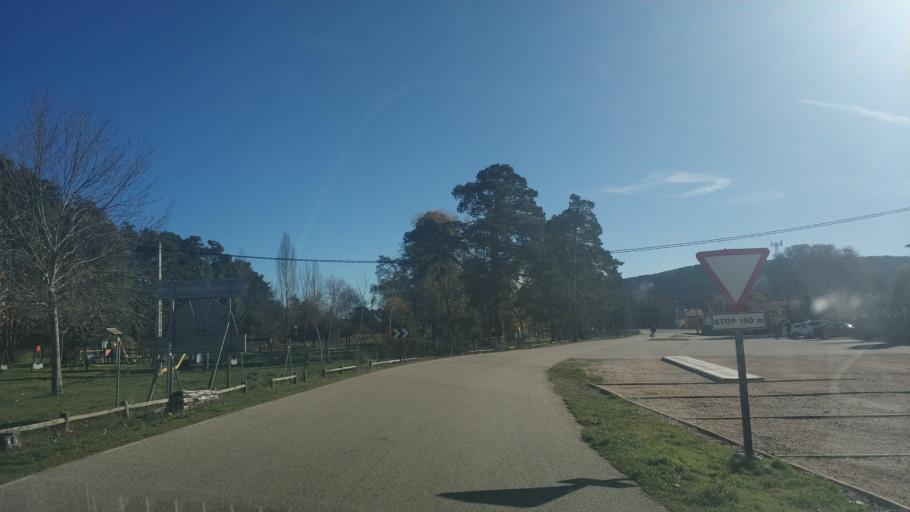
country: ES
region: Castille and Leon
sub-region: Provincia de Soria
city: Vinuesa
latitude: 41.9125
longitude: -2.7594
